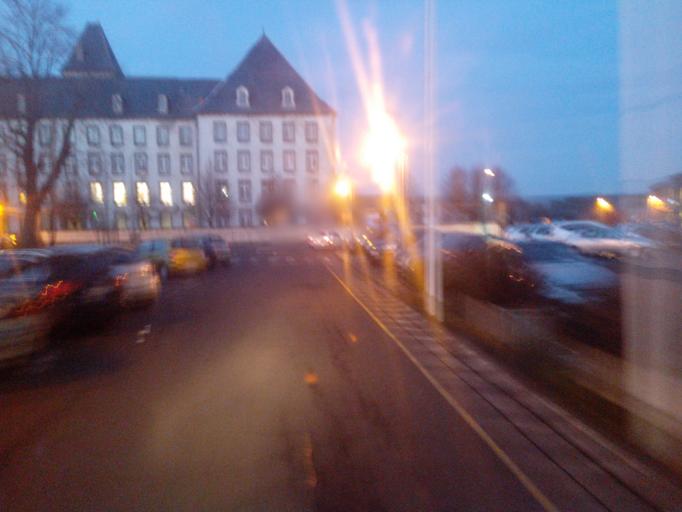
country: FR
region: Auvergne
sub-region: Departement du Cantal
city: Saint-Flour
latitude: 45.0340
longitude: 3.0897
